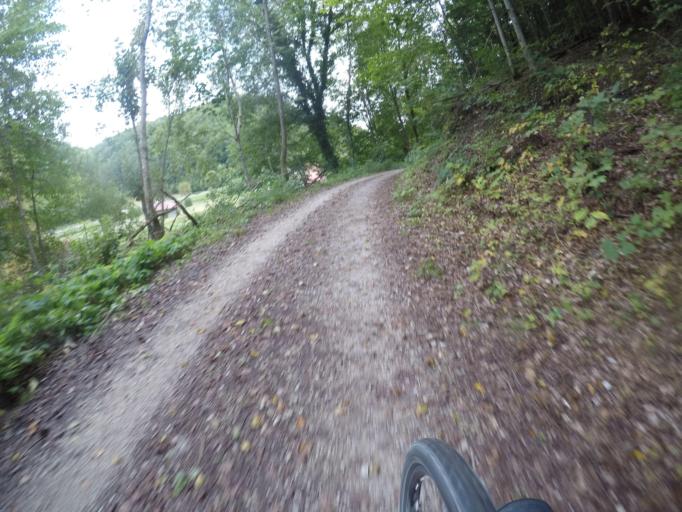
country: DE
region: Baden-Wuerttemberg
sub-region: Tuebingen Region
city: Bad Urach
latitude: 48.4492
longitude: 9.4463
